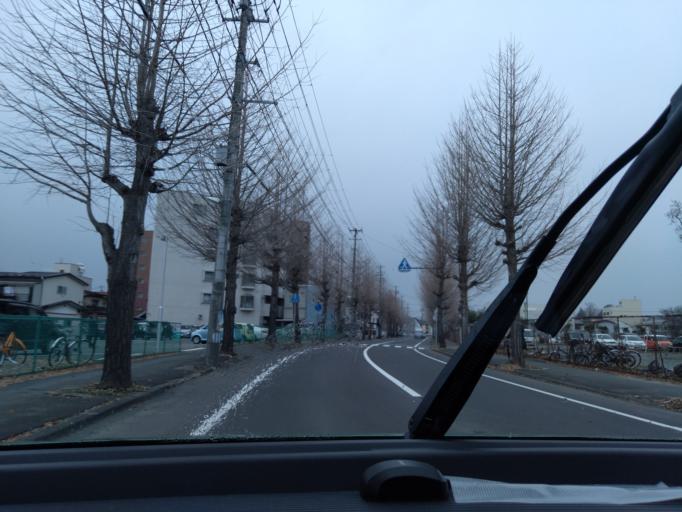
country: JP
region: Iwate
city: Morioka-shi
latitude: 39.7083
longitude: 141.1448
